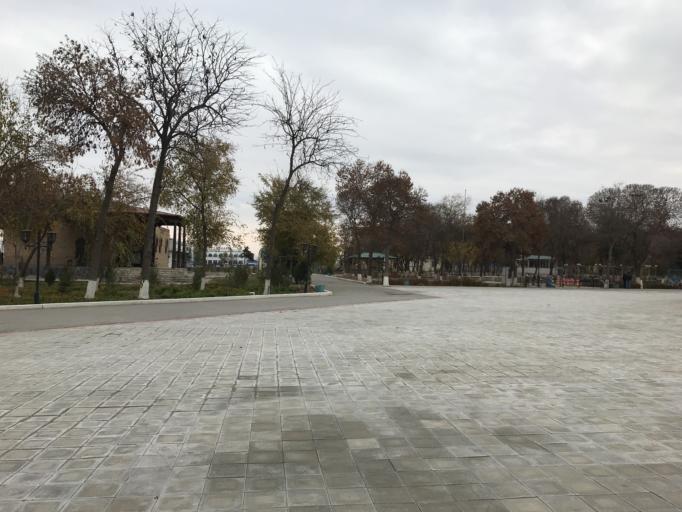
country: UZ
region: Bukhara
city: Kogon
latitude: 39.7247
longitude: 64.5452
